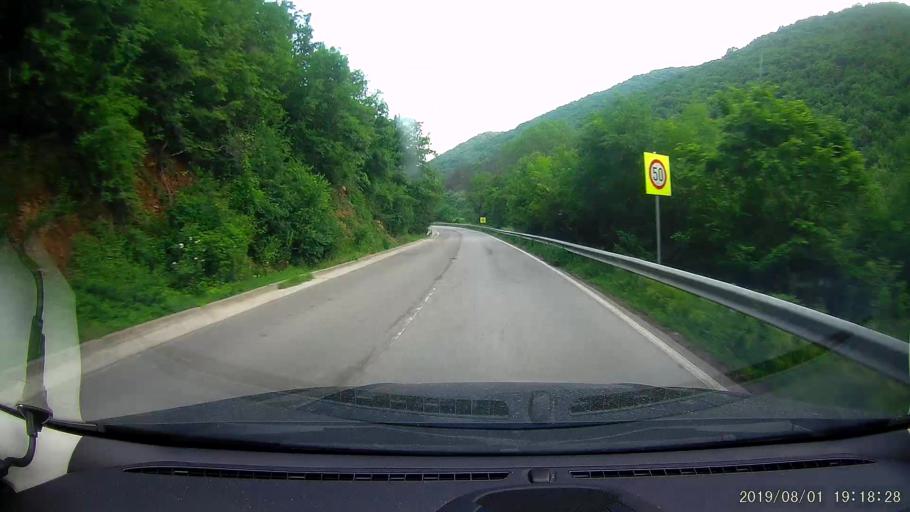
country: BG
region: Shumen
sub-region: Obshtina Smyadovo
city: Smyadovo
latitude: 42.9129
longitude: 26.9401
